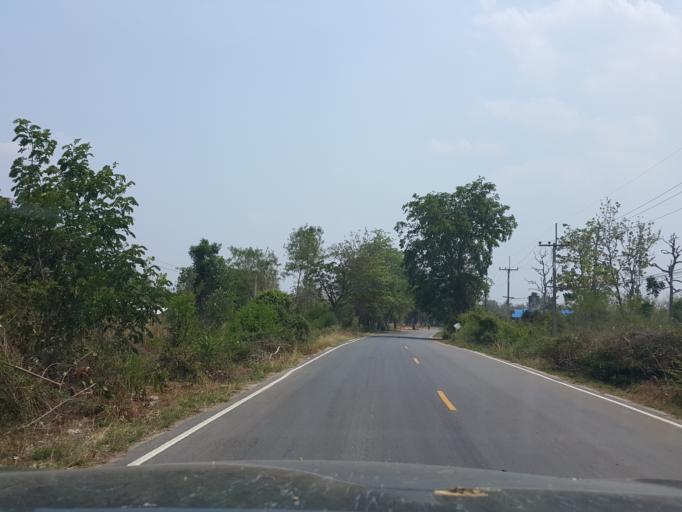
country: TH
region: Lampang
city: Mae Phrik
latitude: 17.4933
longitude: 99.1252
